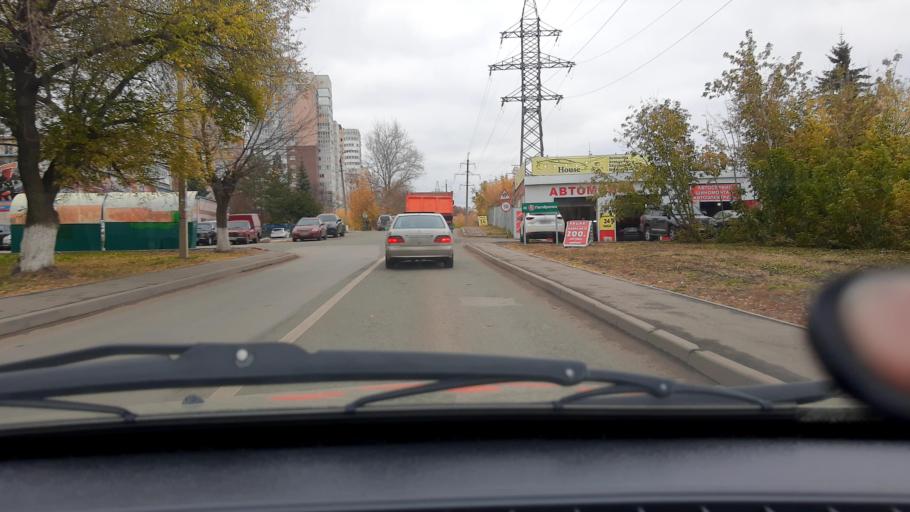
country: RU
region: Bashkortostan
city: Ufa
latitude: 54.7107
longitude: 55.9901
